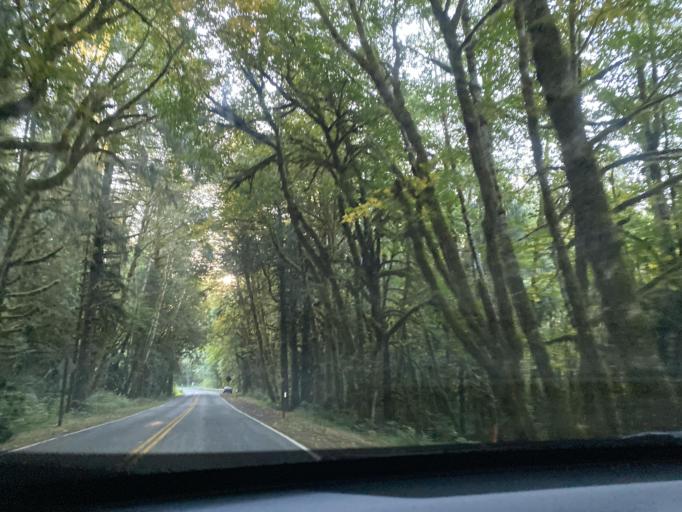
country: US
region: Washington
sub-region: Clallam County
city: Forks
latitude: 47.8228
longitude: -124.2013
